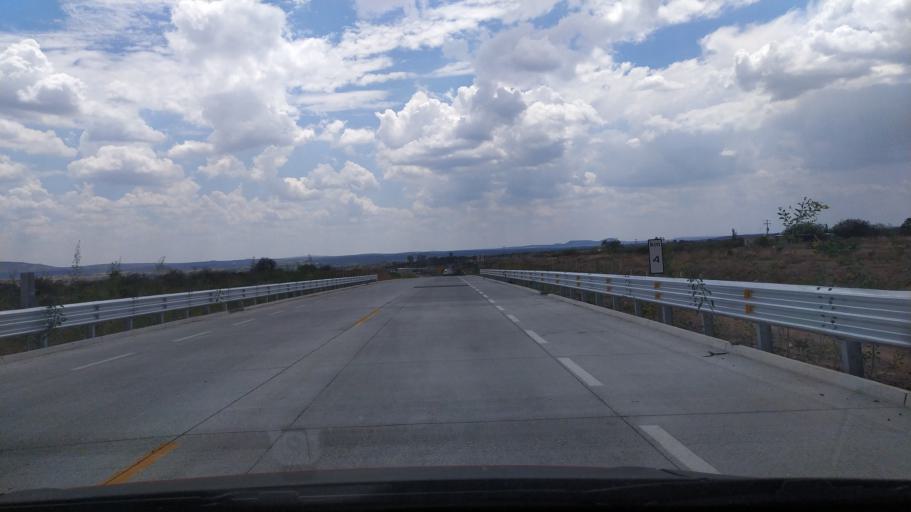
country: MX
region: Guanajuato
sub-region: San Francisco del Rincon
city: Estacion de San Francisco
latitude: 21.0870
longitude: -101.8139
